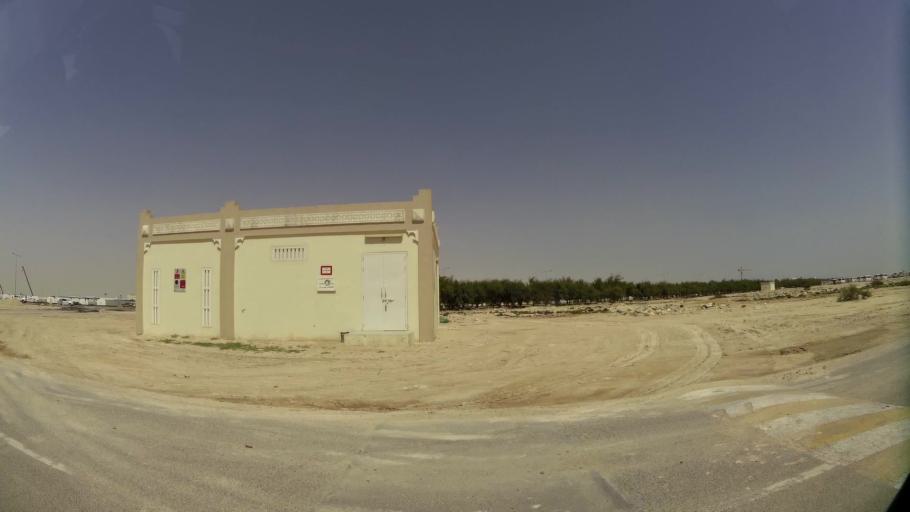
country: QA
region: Baladiyat Umm Salal
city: Umm Salal Muhammad
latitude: 25.3796
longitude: 51.4760
